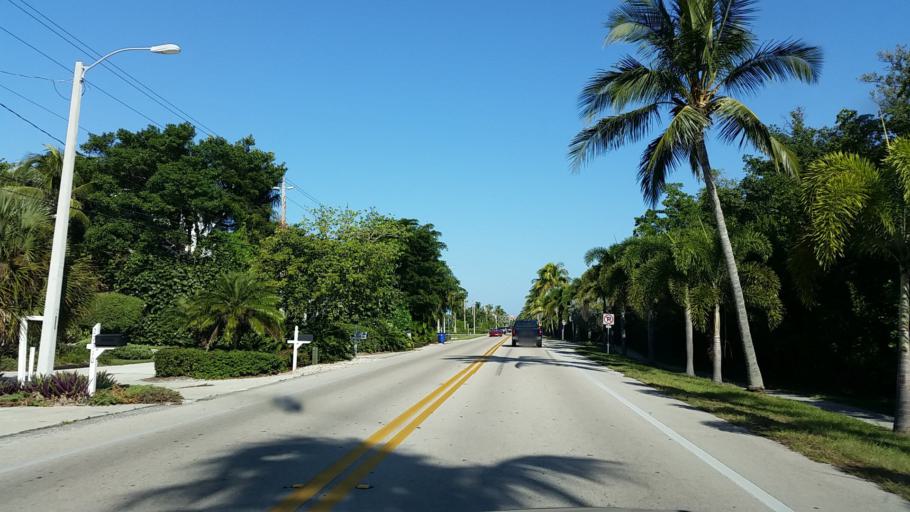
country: US
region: Florida
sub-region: Lee County
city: Bonita Springs
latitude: 26.3408
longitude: -81.8493
